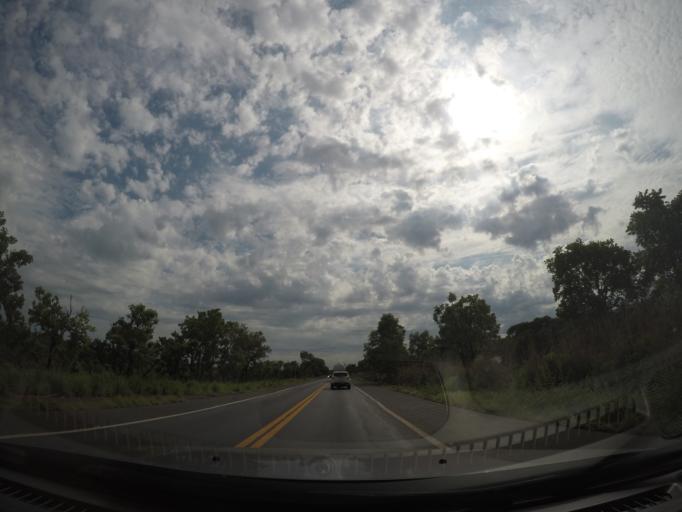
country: BR
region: Goias
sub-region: Formosa
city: Formosa
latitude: -14.9199
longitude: -46.9624
